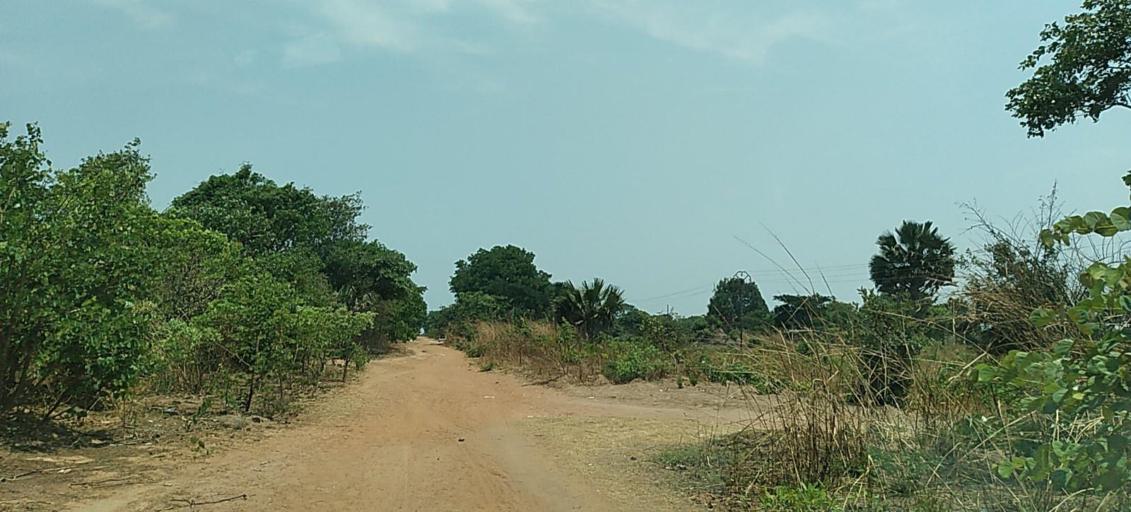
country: ZM
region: Copperbelt
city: Ndola
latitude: -13.0594
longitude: 28.7382
